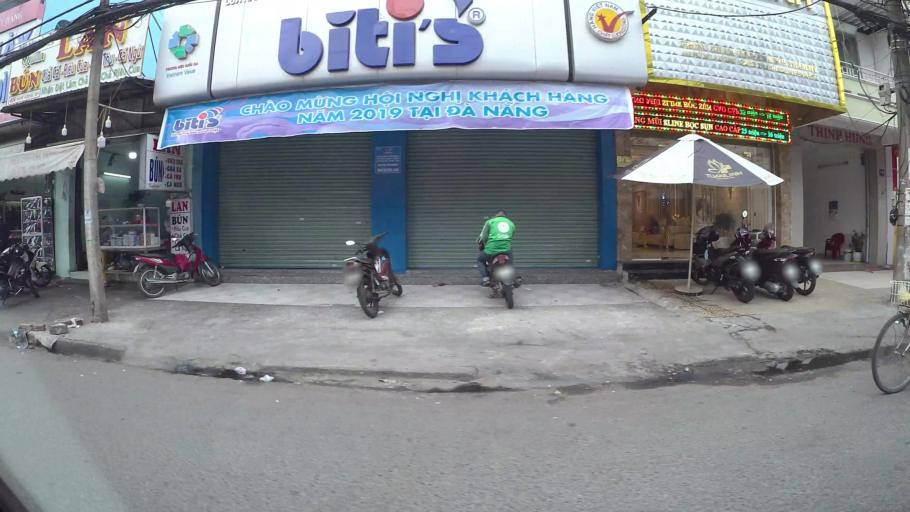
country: VN
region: Da Nang
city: Da Nang
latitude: 16.0667
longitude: 108.2109
